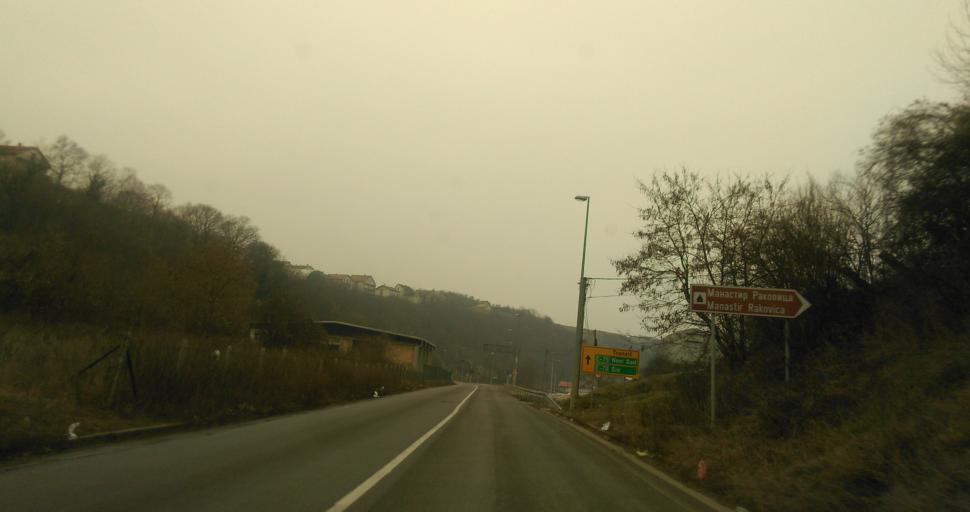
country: RS
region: Central Serbia
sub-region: Belgrade
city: Rakovica
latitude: 44.7232
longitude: 20.4534
